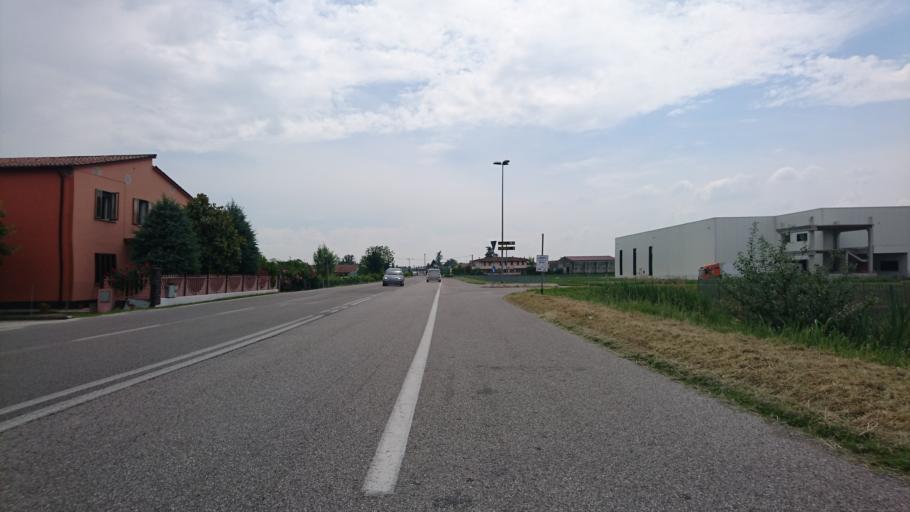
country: IT
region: Veneto
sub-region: Provincia di Rovigo
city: Baruchella
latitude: 45.0732
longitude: 11.4596
